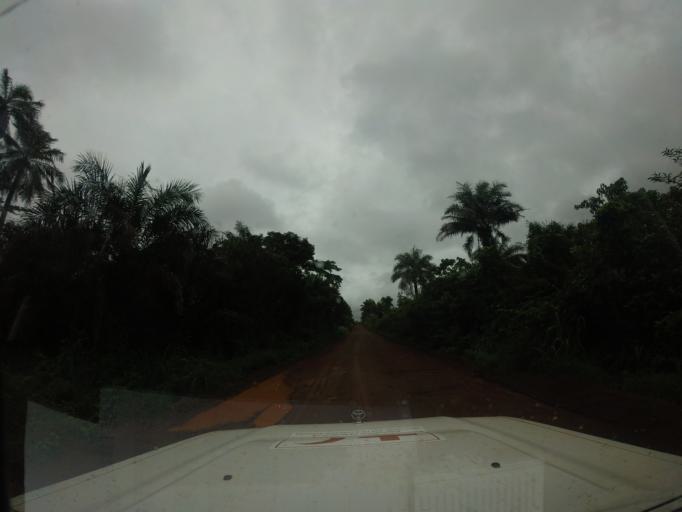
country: SL
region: Northern Province
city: Kambia
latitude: 9.1468
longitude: -12.8814
